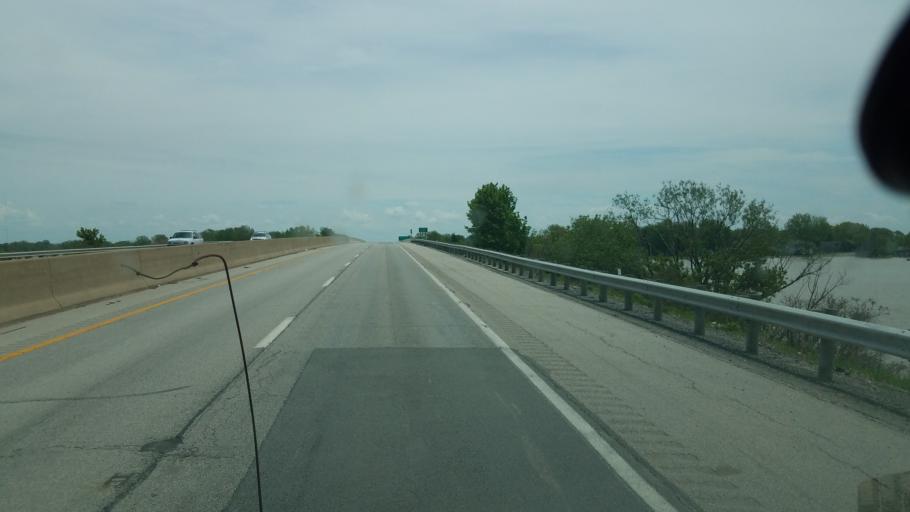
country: US
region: Ohio
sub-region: Ottawa County
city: Port Clinton
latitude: 41.5137
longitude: -82.9930
